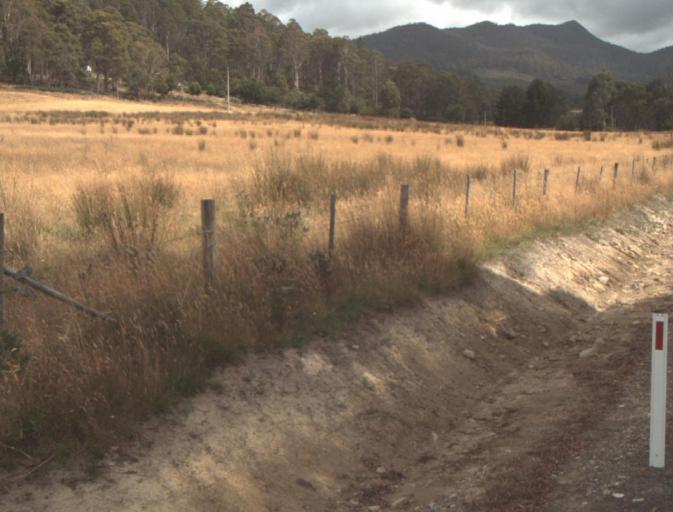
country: AU
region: Tasmania
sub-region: Northern Midlands
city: Evandale
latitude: -41.4623
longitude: 147.4493
